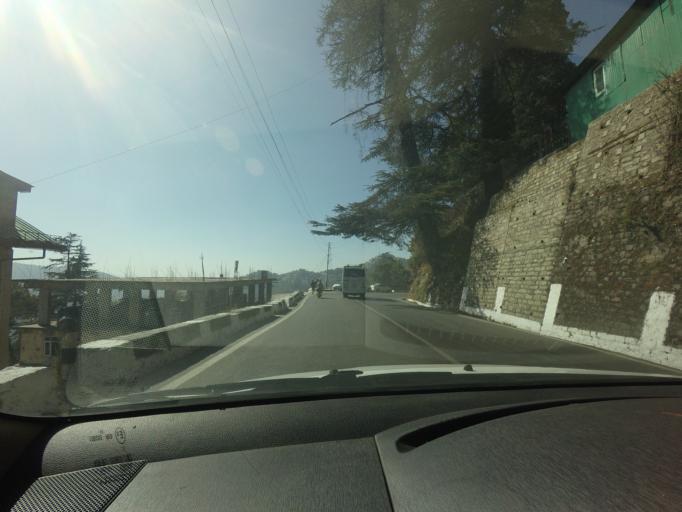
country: IN
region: Himachal Pradesh
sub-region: Shimla
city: Shimla
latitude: 31.1010
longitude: 77.1513
